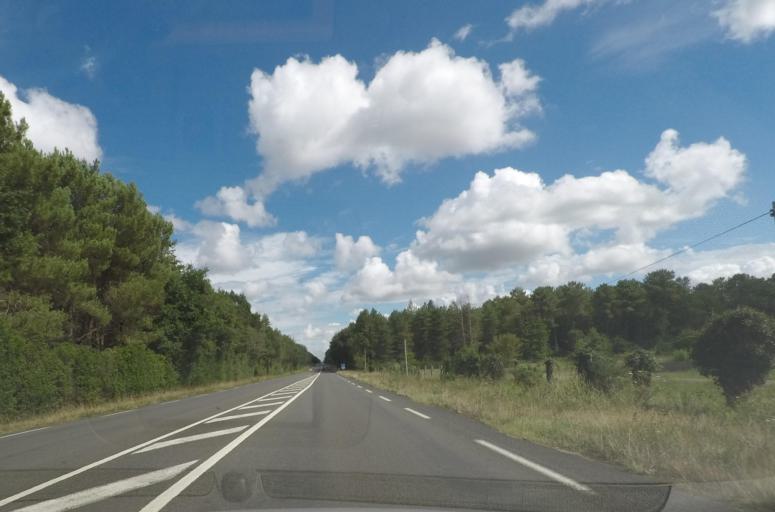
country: FR
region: Pays de la Loire
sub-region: Departement de la Sarthe
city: Cerans-Foulletourte
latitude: 47.7782
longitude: 0.0305
